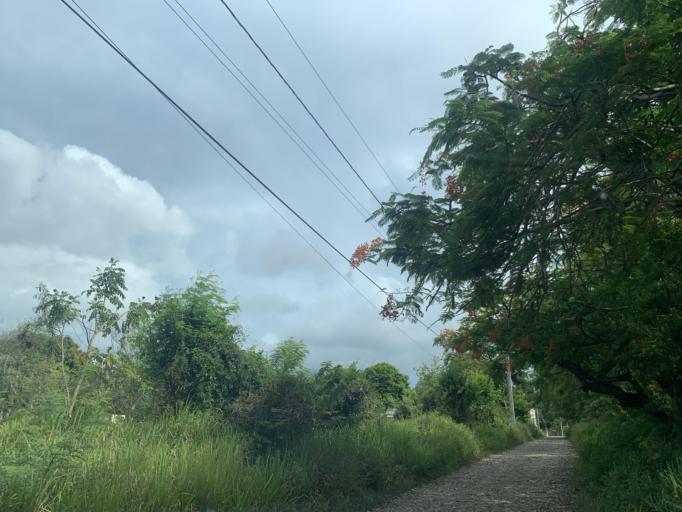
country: DO
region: Puerto Plata
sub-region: Puerto Plata
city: Puerto Plata
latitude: 19.8130
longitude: -70.7202
